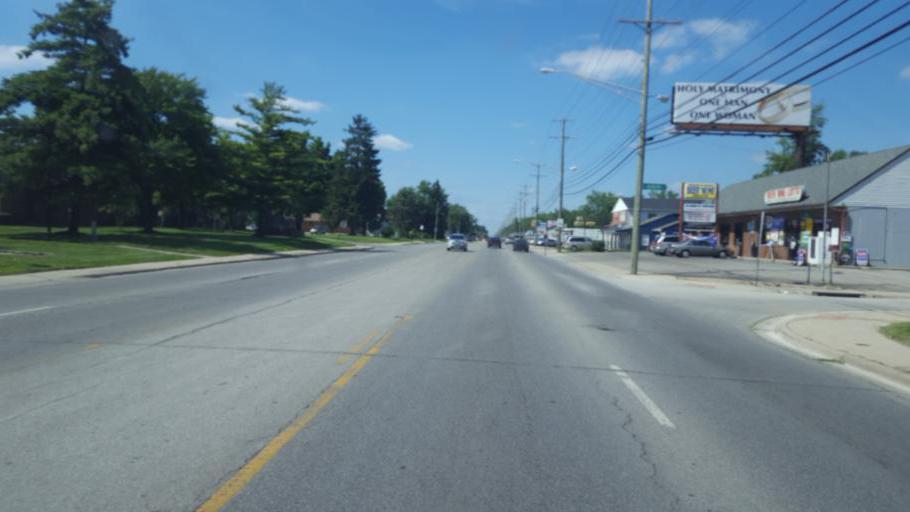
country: US
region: Ohio
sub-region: Franklin County
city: Minerva Park
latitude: 40.0630
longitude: -82.9527
